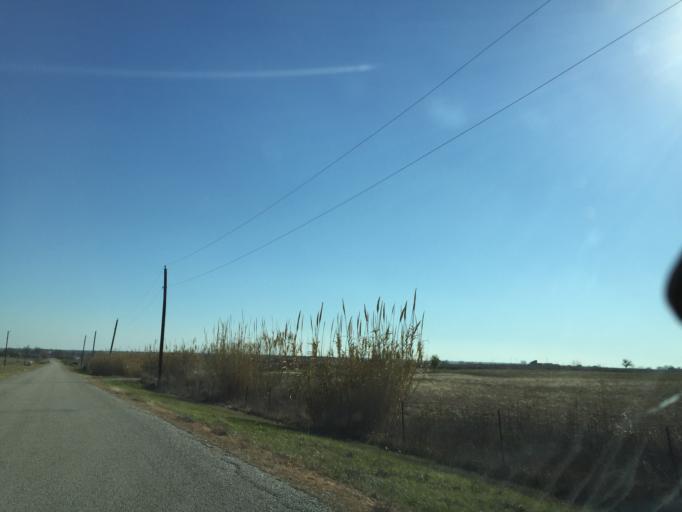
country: US
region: Texas
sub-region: Williamson County
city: Taylor
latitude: 30.5647
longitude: -97.3075
